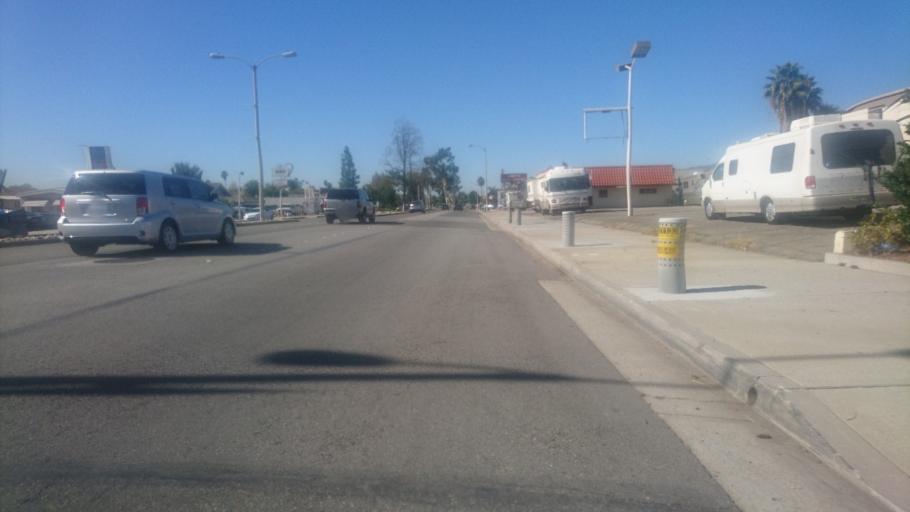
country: US
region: California
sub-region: Los Angeles County
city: Glendora
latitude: 34.1288
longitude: -117.8533
